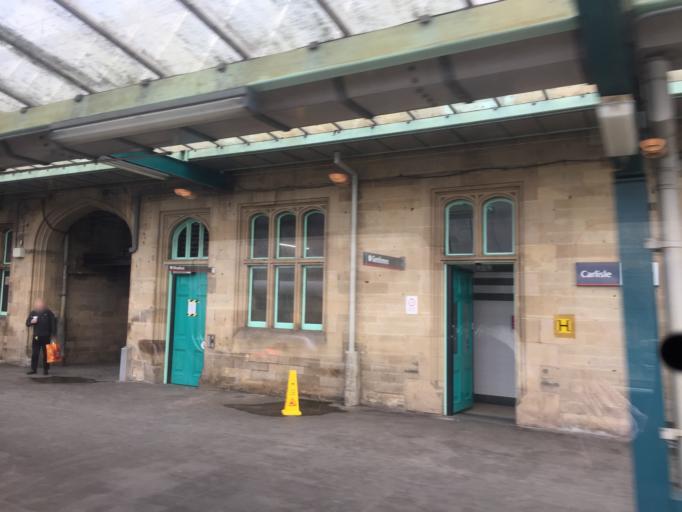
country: GB
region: England
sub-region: Cumbria
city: Carlisle
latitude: 54.8900
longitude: -2.9328
